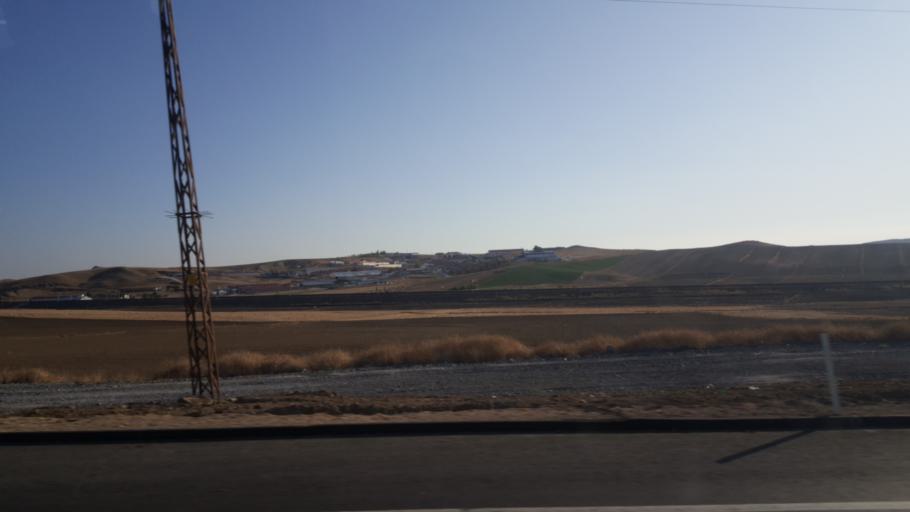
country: TR
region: Ankara
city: Polatli
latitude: 39.5727
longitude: 32.1043
